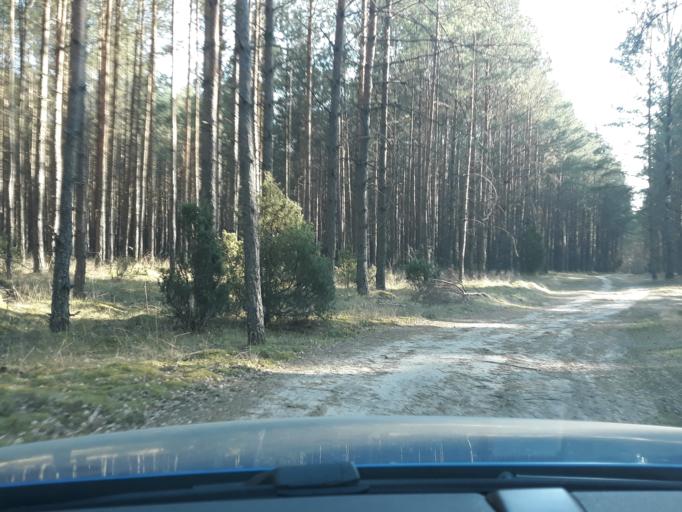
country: PL
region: Pomeranian Voivodeship
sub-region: Powiat bytowski
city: Lipnica
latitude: 53.9049
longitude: 17.4949
